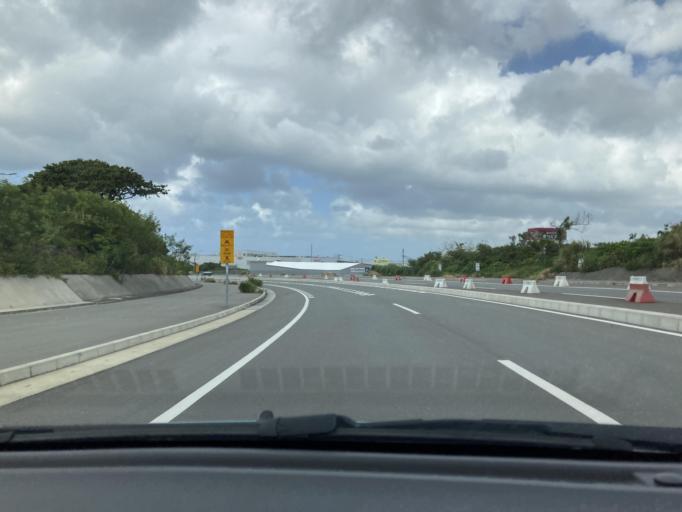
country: JP
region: Okinawa
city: Ginowan
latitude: 26.2673
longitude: 127.7097
